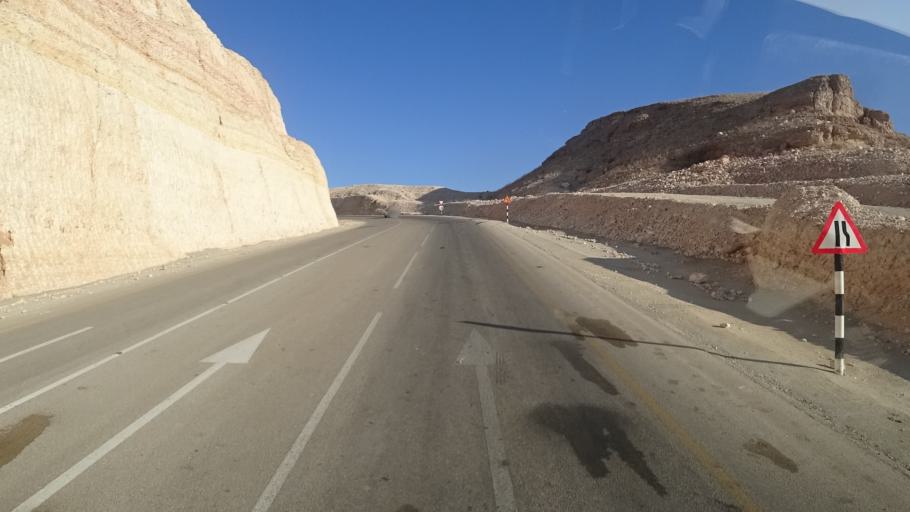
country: YE
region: Al Mahrah
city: Hawf
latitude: 17.0928
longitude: 53.0615
